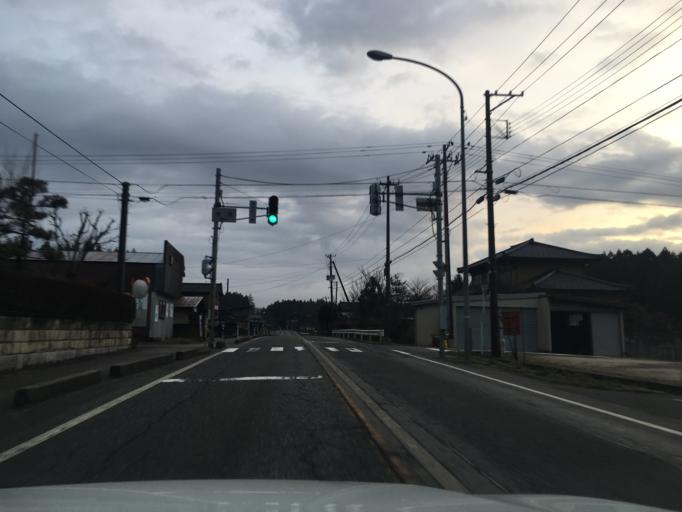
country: JP
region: Niigata
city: Murakami
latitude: 38.2949
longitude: 139.5316
